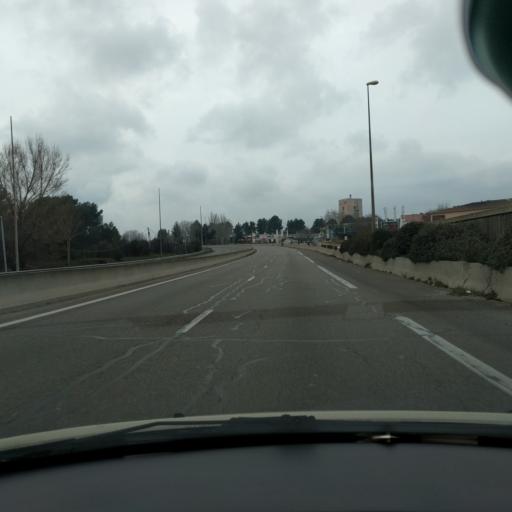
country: FR
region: Provence-Alpes-Cote d'Azur
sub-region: Departement des Bouches-du-Rhone
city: Gardanne
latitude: 43.4543
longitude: 5.4557
